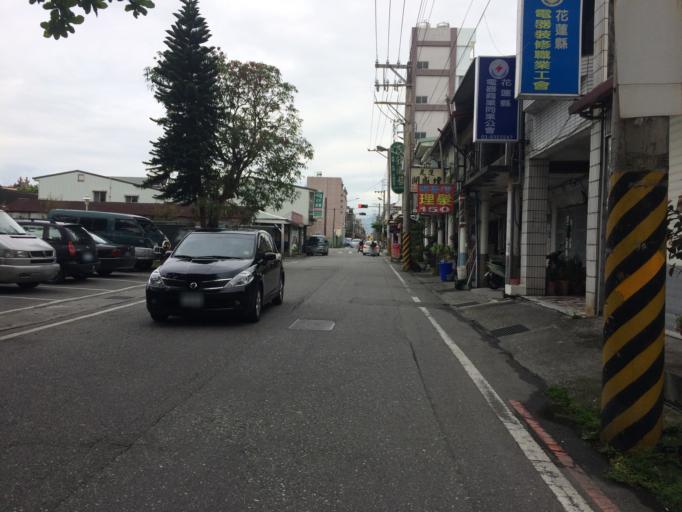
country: TW
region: Taiwan
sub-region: Hualien
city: Hualian
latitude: 23.9723
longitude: 121.6057
